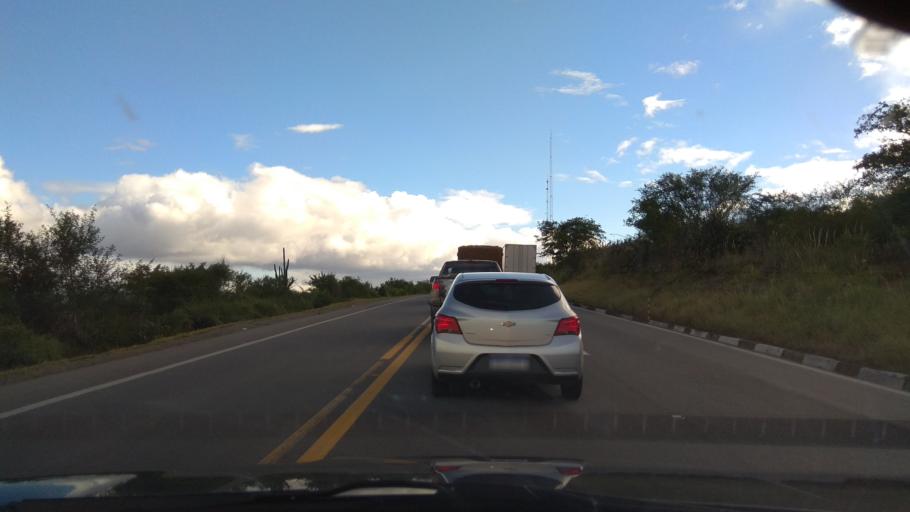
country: BR
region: Bahia
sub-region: Castro Alves
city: Castro Alves
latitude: -12.6538
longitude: -39.6150
